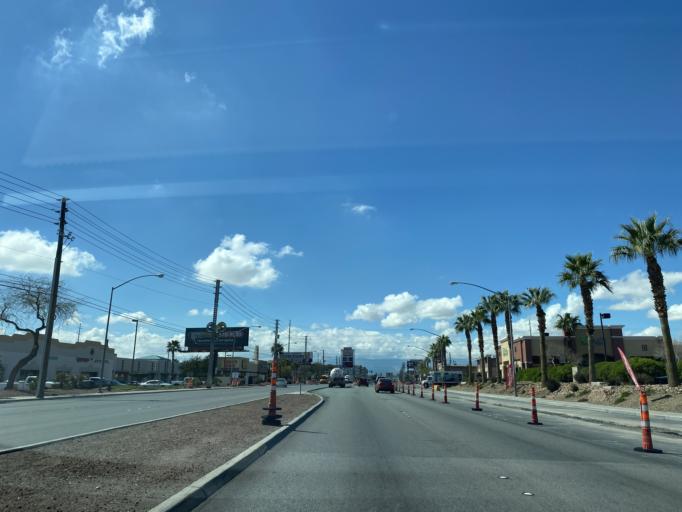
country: US
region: Nevada
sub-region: Clark County
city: North Las Vegas
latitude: 36.2400
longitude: -115.1131
